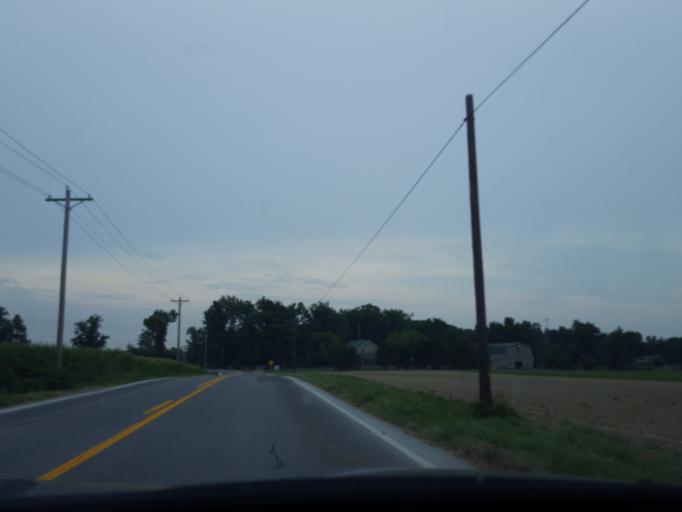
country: US
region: Maryland
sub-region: Saint Mary's County
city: Charlotte Hall
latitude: 38.4557
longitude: -76.7834
